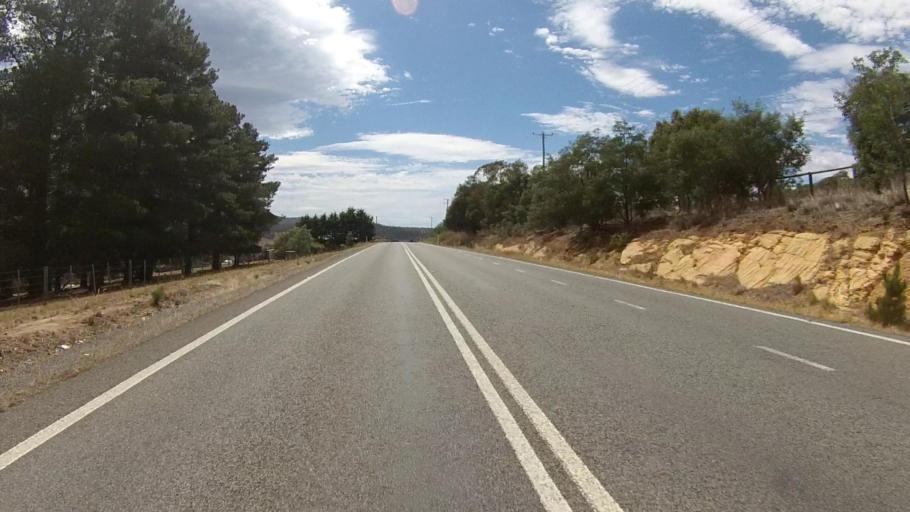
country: AU
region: Tasmania
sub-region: Brighton
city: Old Beach
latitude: -42.6702
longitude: 147.3666
